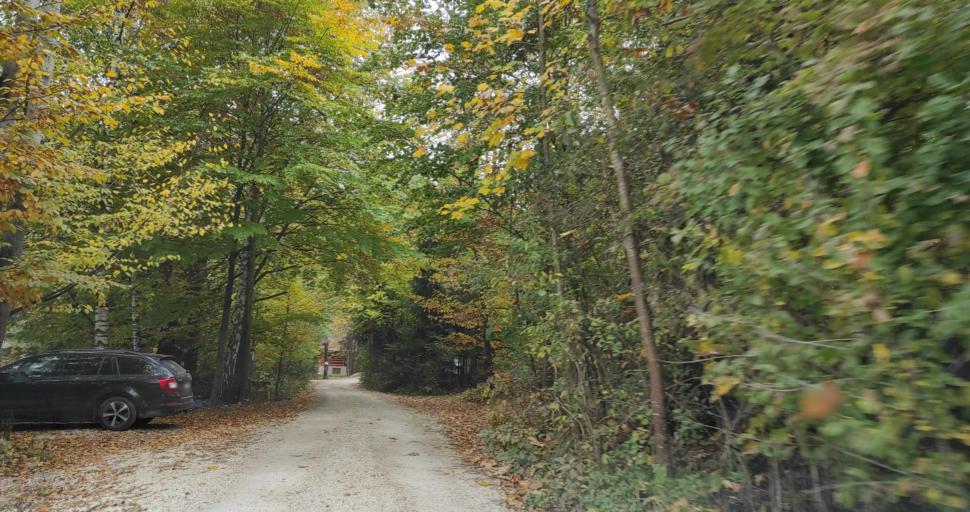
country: SK
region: Kosicky
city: Gelnica
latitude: 48.8825
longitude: 21.0488
